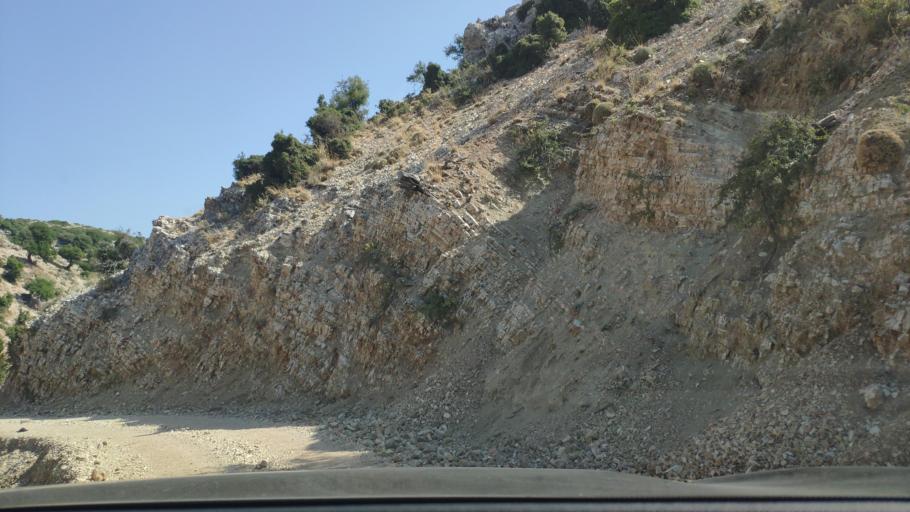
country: GR
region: West Greece
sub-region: Nomos Aitolias kai Akarnanias
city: Monastirakion
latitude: 38.8022
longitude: 20.9967
